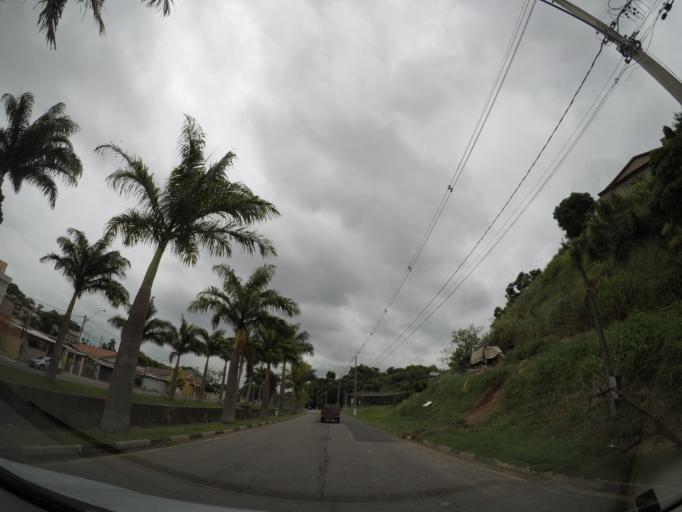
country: BR
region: Sao Paulo
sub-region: Vinhedo
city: Vinhedo
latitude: -23.0159
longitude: -46.9806
